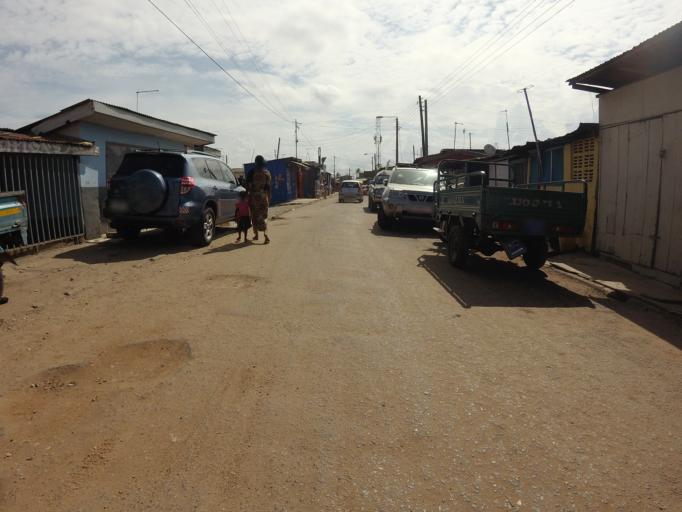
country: GH
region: Greater Accra
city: Accra
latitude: 5.5941
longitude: -0.1921
